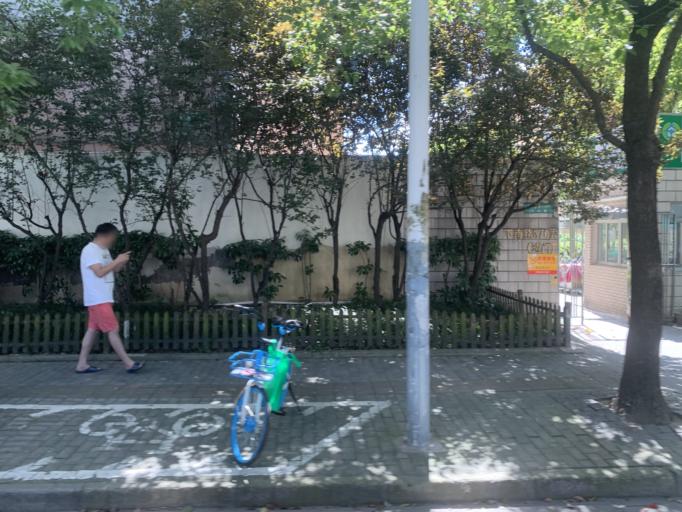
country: CN
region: Shanghai Shi
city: Huamu
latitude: 31.1720
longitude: 121.5369
